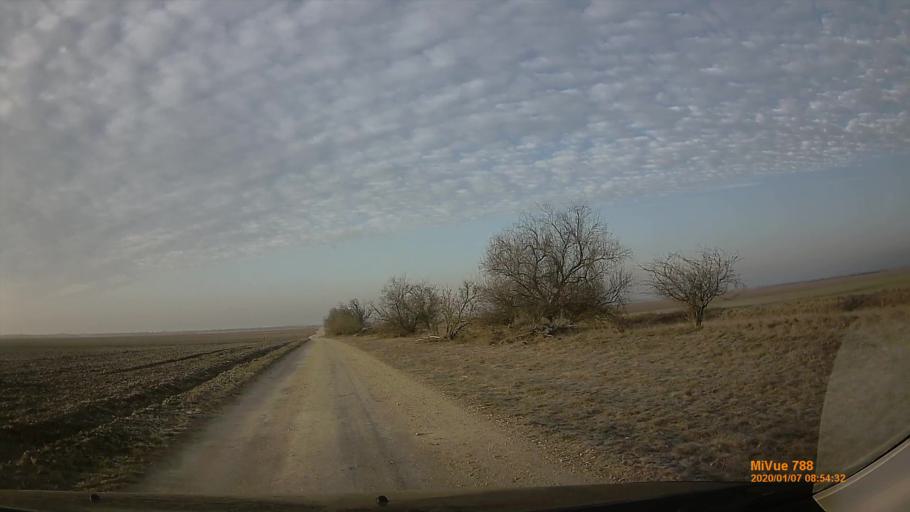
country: HU
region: Gyor-Moson-Sopron
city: Rajka
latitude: 47.9942
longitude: 17.1786
